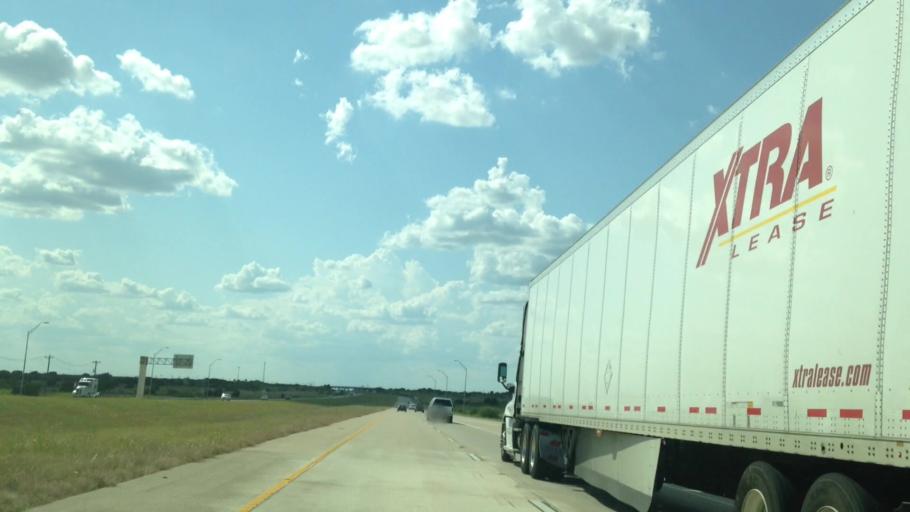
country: US
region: Texas
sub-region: Travis County
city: Onion Creek
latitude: 30.0851
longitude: -97.7377
